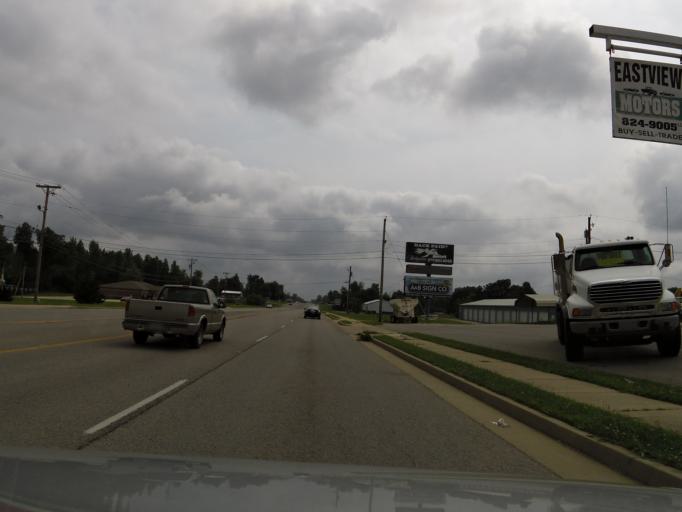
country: US
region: Kentucky
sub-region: Hopkins County
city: Madisonville
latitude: 37.3257
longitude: -87.4559
